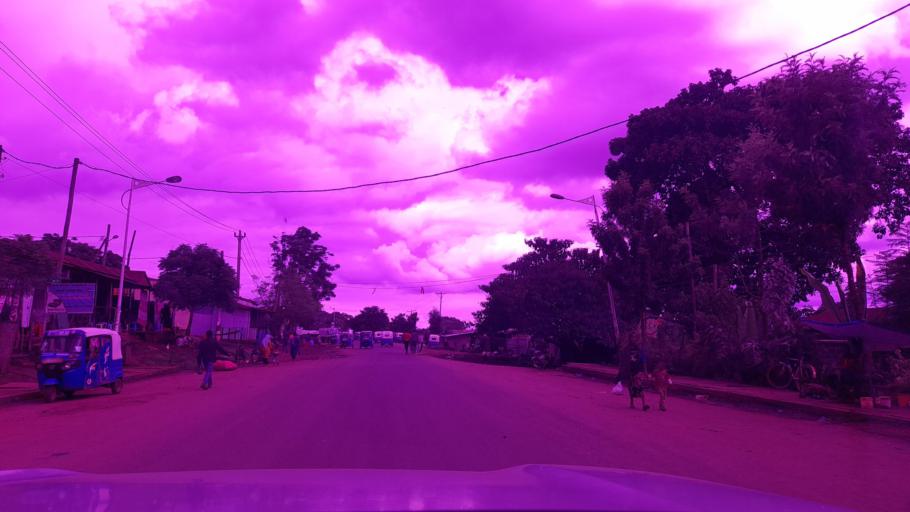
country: ET
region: Oromiya
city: Jima
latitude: 7.6716
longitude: 36.8554
